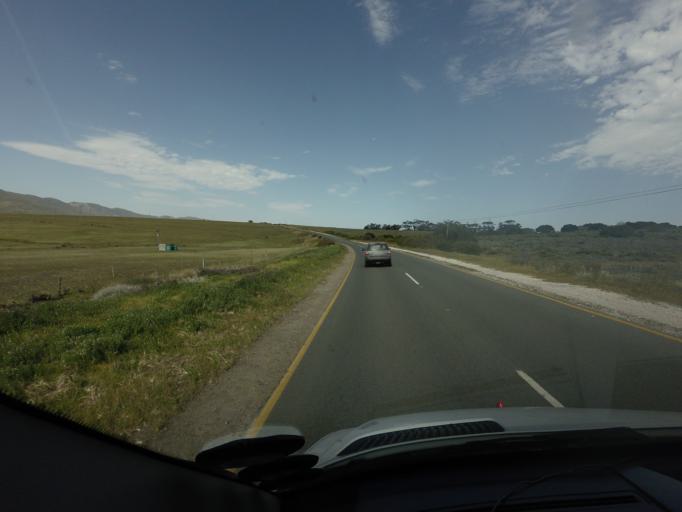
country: ZA
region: Western Cape
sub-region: Overberg District Municipality
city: Caledon
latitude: -34.4424
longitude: 19.4780
